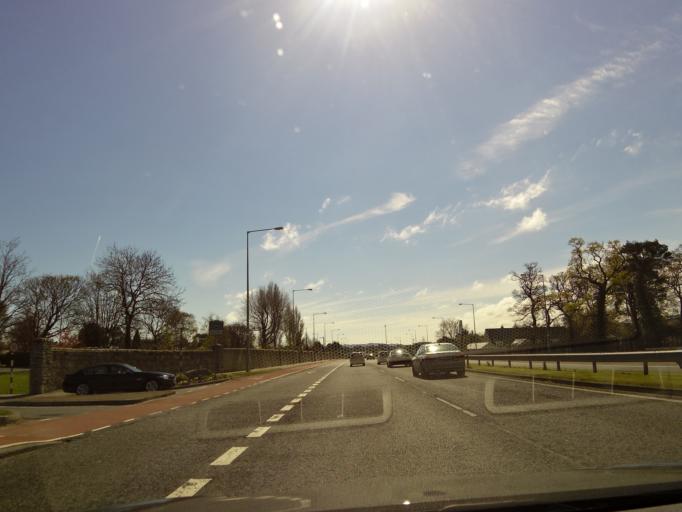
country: IE
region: Leinster
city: Loughlinstown
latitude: 53.2540
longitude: -6.1436
